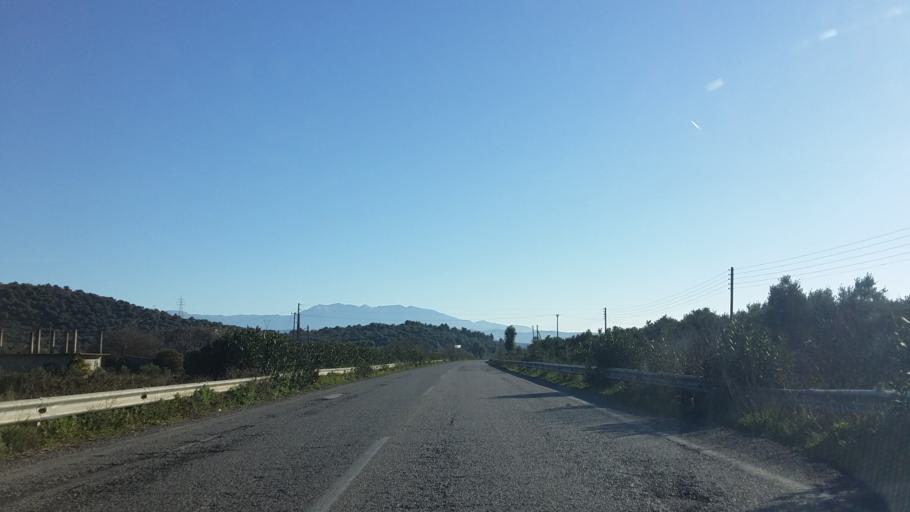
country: GR
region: West Greece
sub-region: Nomos Aitolias kai Akarnanias
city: Lepenou
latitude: 38.6864
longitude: 21.2478
